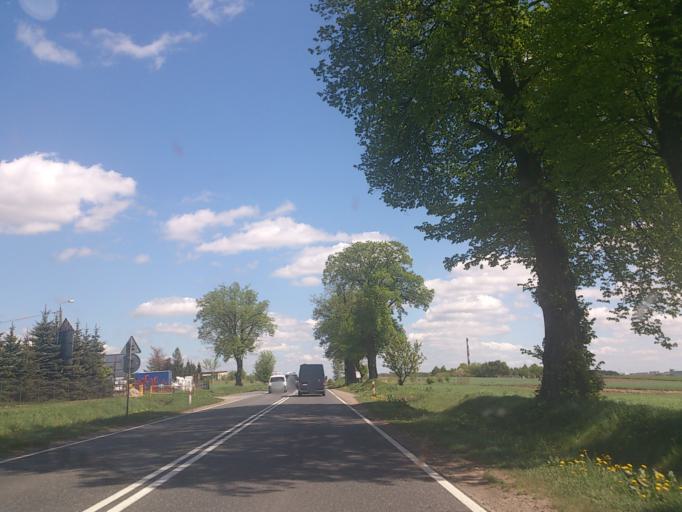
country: PL
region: Podlasie
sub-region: Lomza
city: Lomza
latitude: 53.1694
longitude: 21.9988
